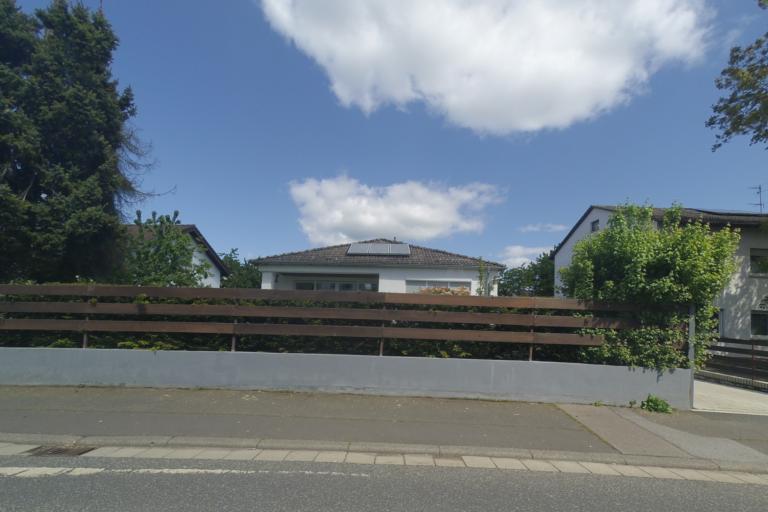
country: DE
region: Hesse
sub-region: Regierungsbezirk Darmstadt
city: Karben
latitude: 50.2417
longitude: 8.7227
